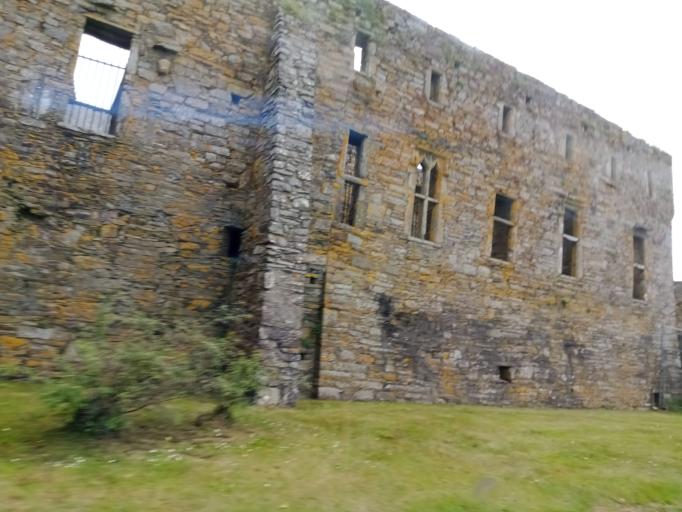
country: IE
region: Munster
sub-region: County Cork
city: Bandon
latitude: 51.6432
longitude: -8.7630
